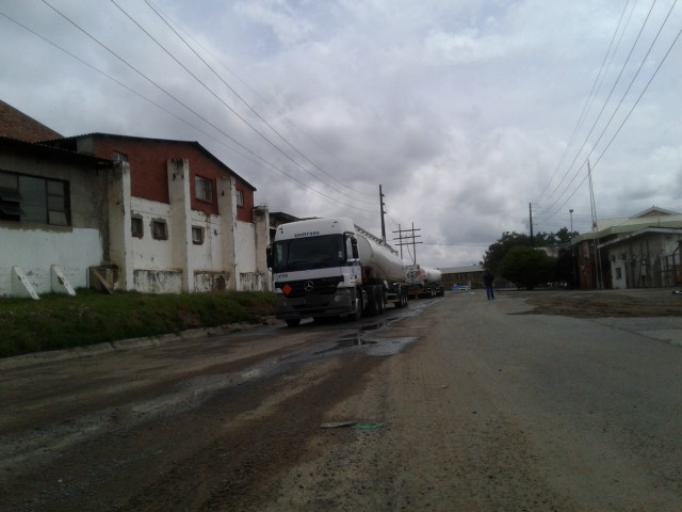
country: LS
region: Maseru
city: Maseru
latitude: -29.2979
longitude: 27.4744
